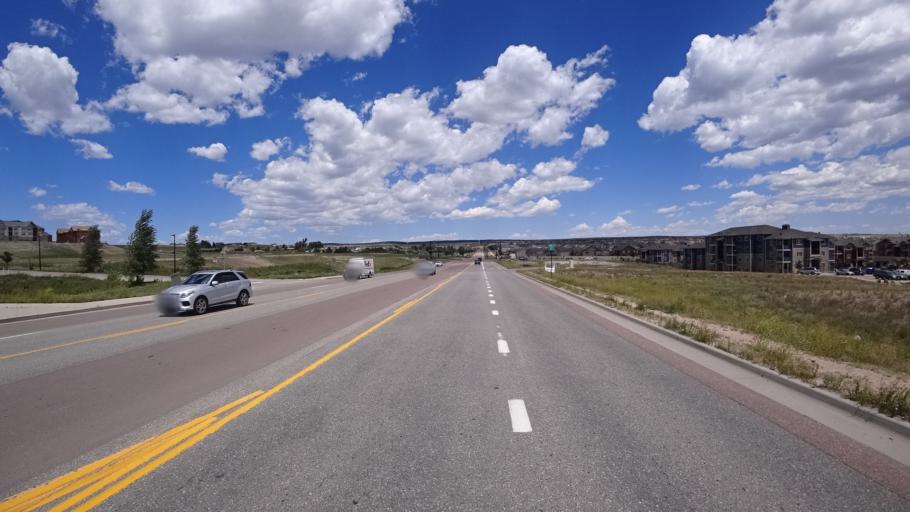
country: US
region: Colorado
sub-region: El Paso County
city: Black Forest
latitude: 38.9419
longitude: -104.7009
